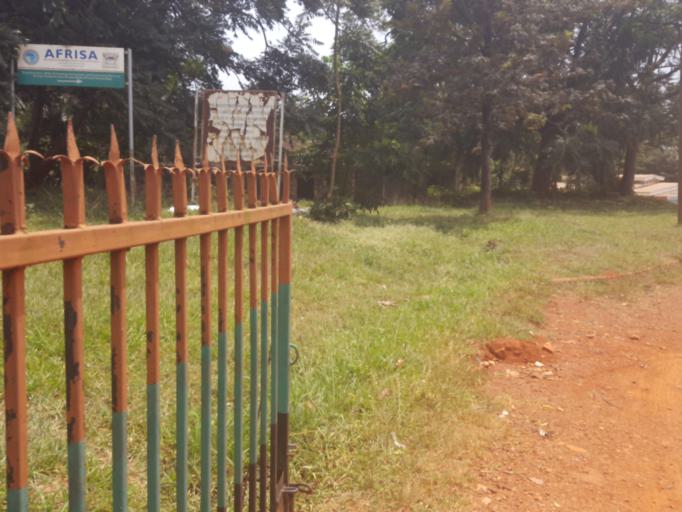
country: UG
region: Central Region
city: Kampala Central Division
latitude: 0.3401
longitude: 32.5673
